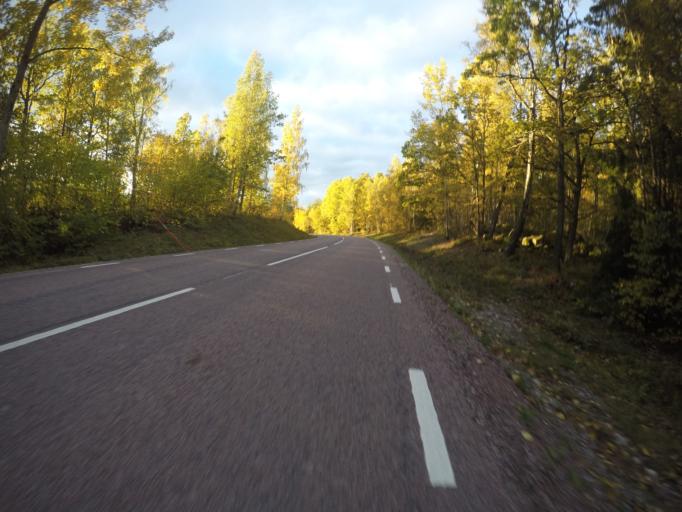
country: SE
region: Vaestmanland
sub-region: Arboga Kommun
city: Tyringe
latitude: 59.3142
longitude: 15.9822
